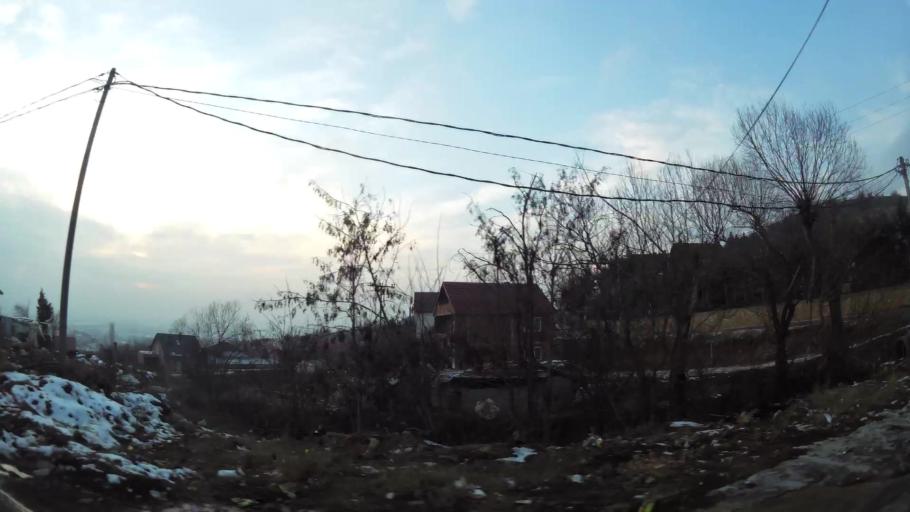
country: MK
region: Aracinovo
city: Arachinovo
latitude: 42.0312
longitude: 21.5583
